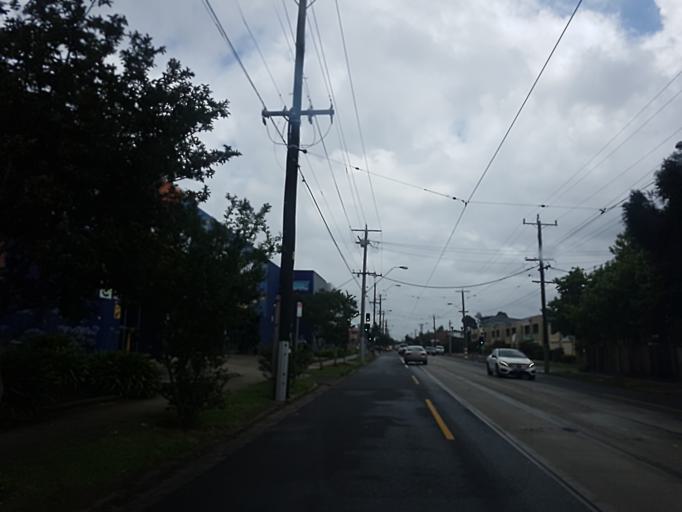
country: AU
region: Victoria
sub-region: Maribyrnong
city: Maribyrnong
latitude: -37.7878
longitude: 144.8901
